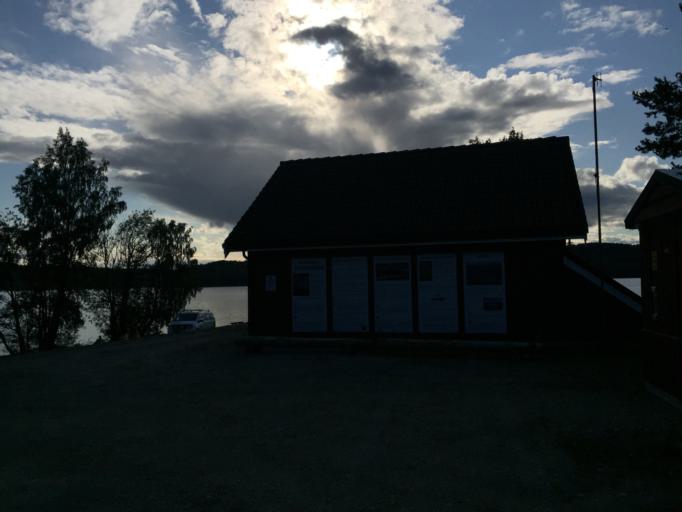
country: NO
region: Ostfold
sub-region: Trogstad
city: Skjonhaug
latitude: 59.6687
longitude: 11.2500
